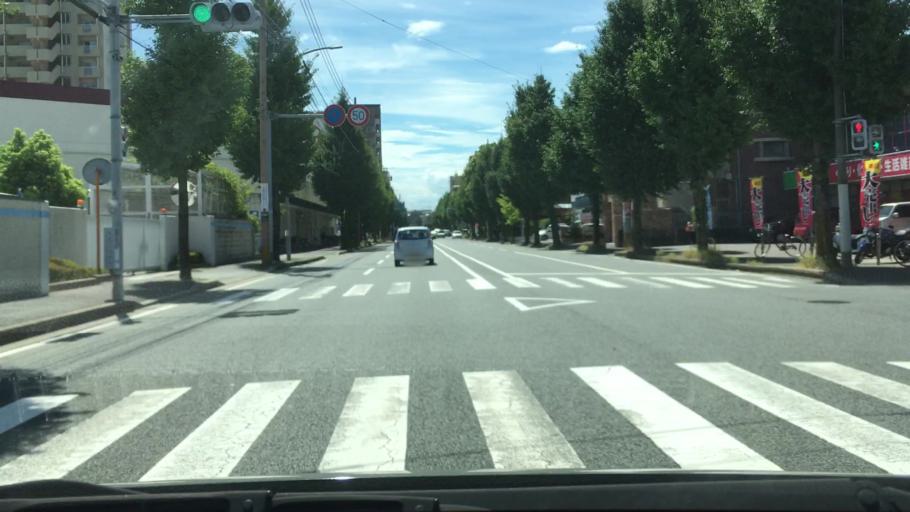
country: JP
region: Fukuoka
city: Fukuoka-shi
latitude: 33.5695
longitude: 130.4250
